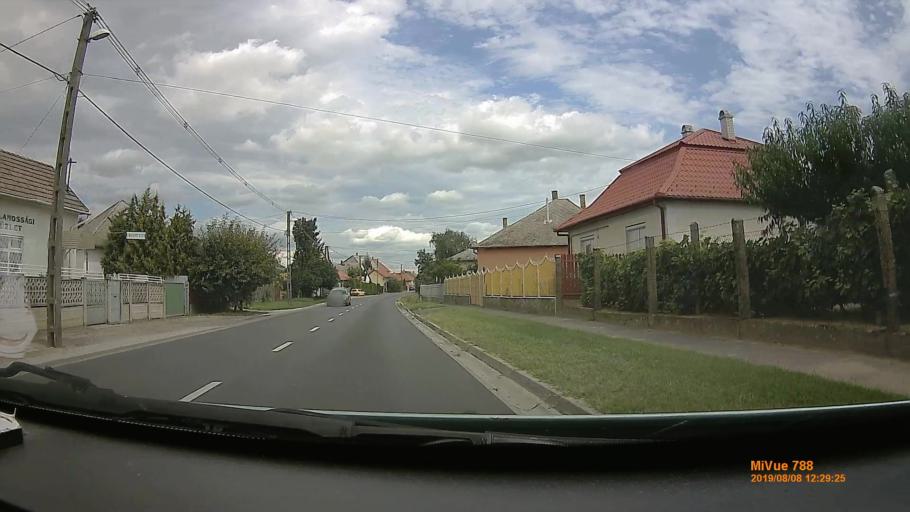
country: HU
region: Szabolcs-Szatmar-Bereg
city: Nyirbator
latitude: 47.8350
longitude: 22.1190
